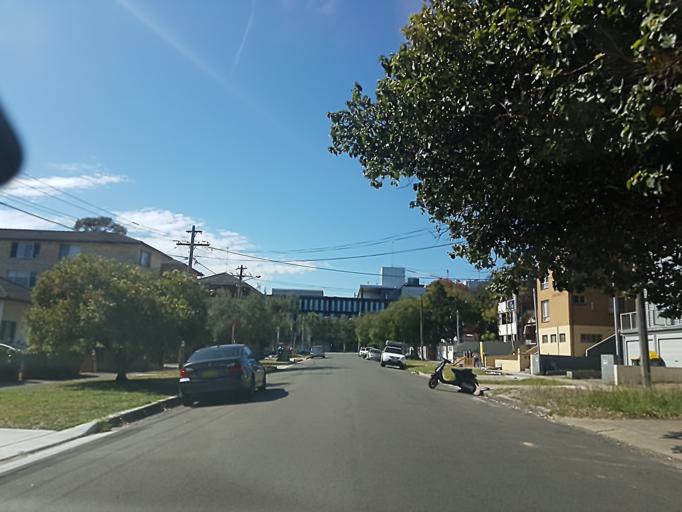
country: AU
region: New South Wales
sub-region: Randwick
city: Kingsford
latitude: -33.9210
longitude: 151.2301
